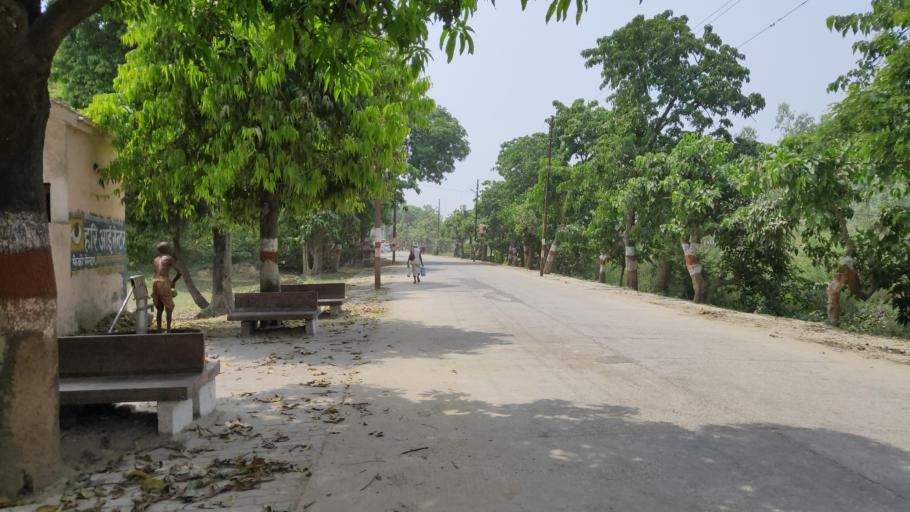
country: IN
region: Uttar Pradesh
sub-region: Faizabad
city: Ayodhya
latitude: 26.7858
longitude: 82.1798
